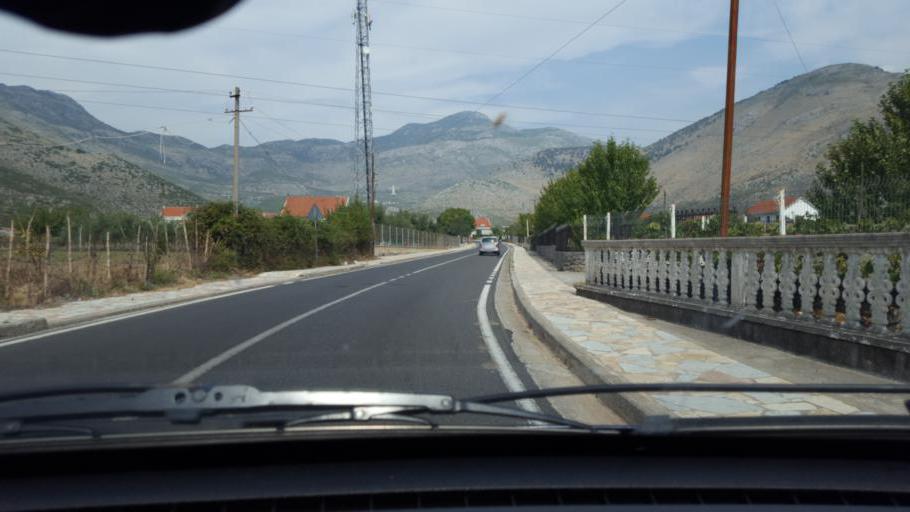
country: AL
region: Shkoder
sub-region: Rrethi i Malesia e Madhe
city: Hot
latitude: 42.3417
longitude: 19.4381
